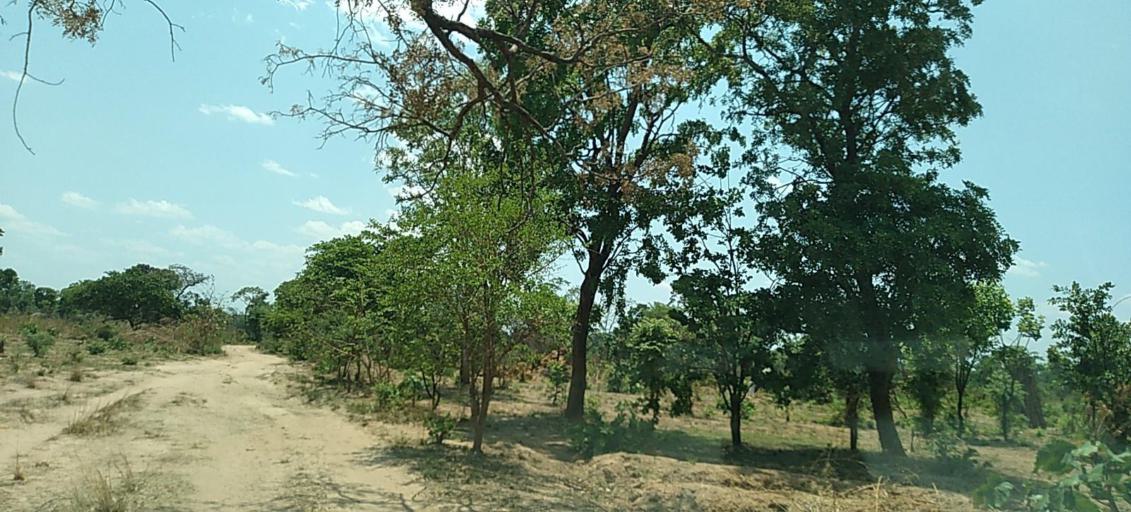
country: ZM
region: Central
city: Kapiri Mposhi
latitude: -13.6346
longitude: 28.7510
